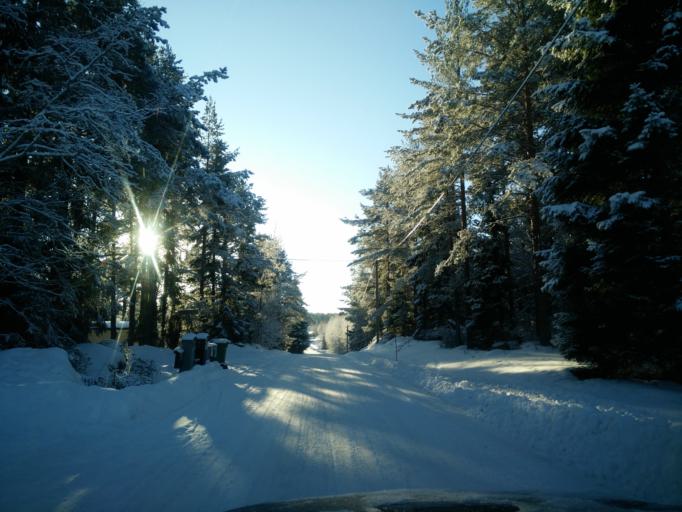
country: SE
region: Vaesternorrland
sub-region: Sundsvalls Kommun
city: Njurundabommen
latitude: 62.2280
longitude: 17.4986
